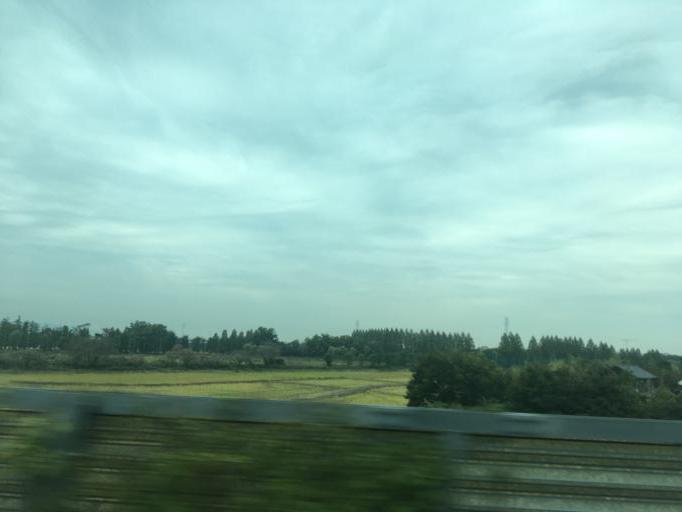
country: JP
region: Saitama
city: Kamifukuoka
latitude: 35.9113
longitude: 139.5550
